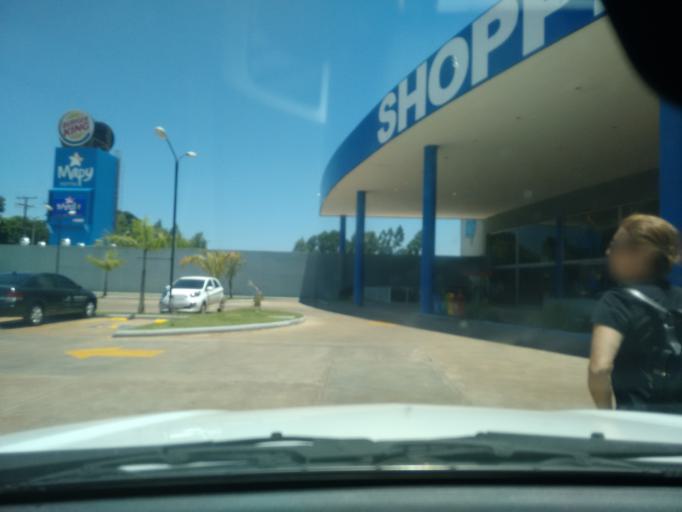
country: PY
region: Canindeyu
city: Salto del Guaira
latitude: -24.0427
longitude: -54.3135
